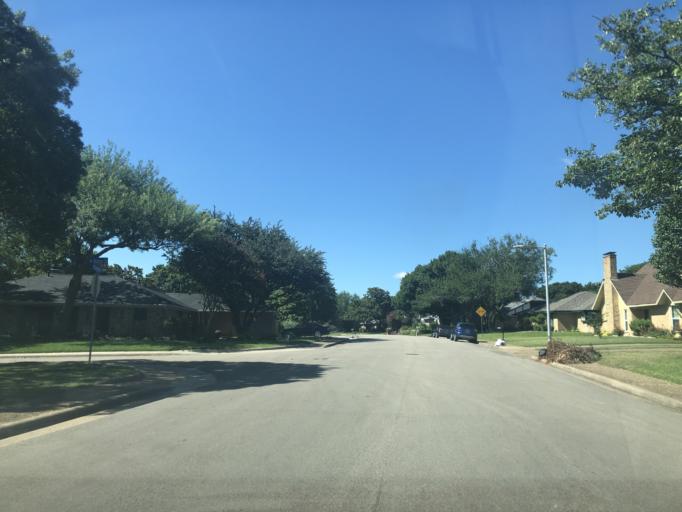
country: US
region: Texas
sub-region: Dallas County
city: Duncanville
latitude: 32.6532
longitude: -96.9335
